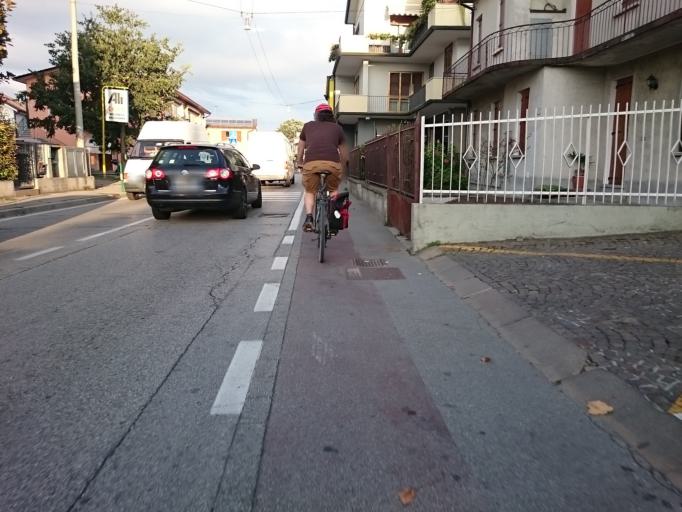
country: IT
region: Veneto
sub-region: Provincia di Padova
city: Noventa
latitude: 45.4011
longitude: 11.9429
